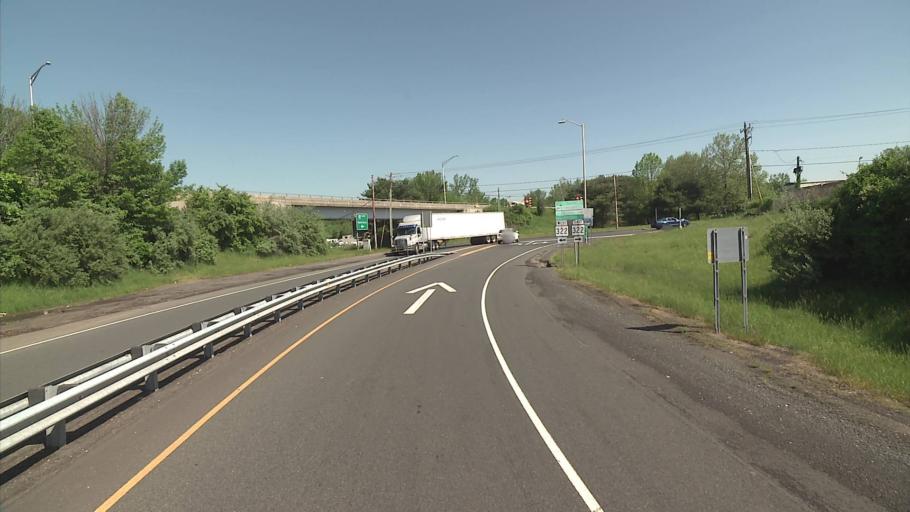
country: US
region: Connecticut
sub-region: New Haven County
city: Cheshire Village
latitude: 41.5626
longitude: -72.9167
